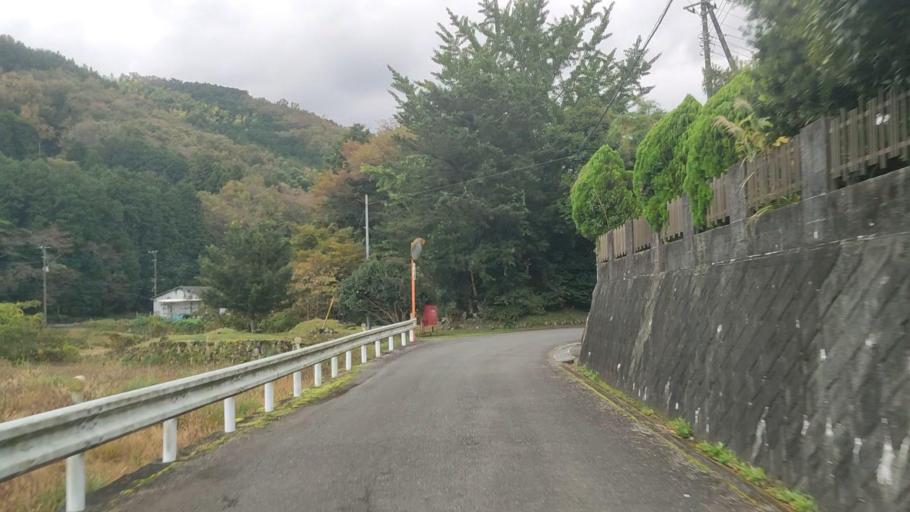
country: JP
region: Shizuoka
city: Ito
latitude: 34.9281
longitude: 138.9895
